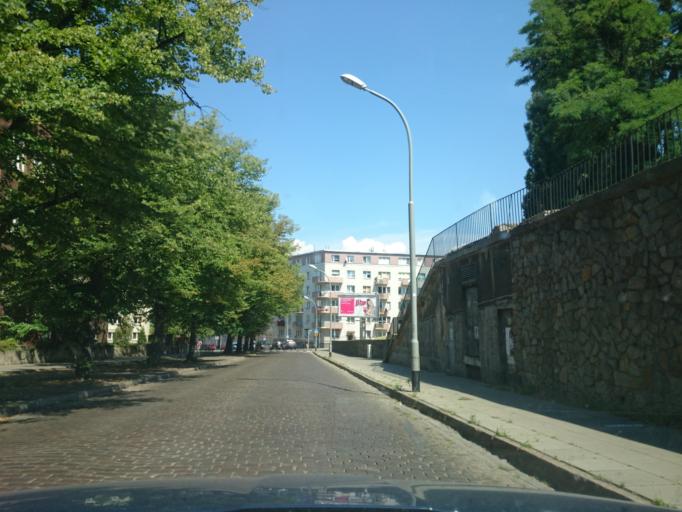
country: PL
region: West Pomeranian Voivodeship
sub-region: Szczecin
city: Szczecin
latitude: 53.4394
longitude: 14.5479
